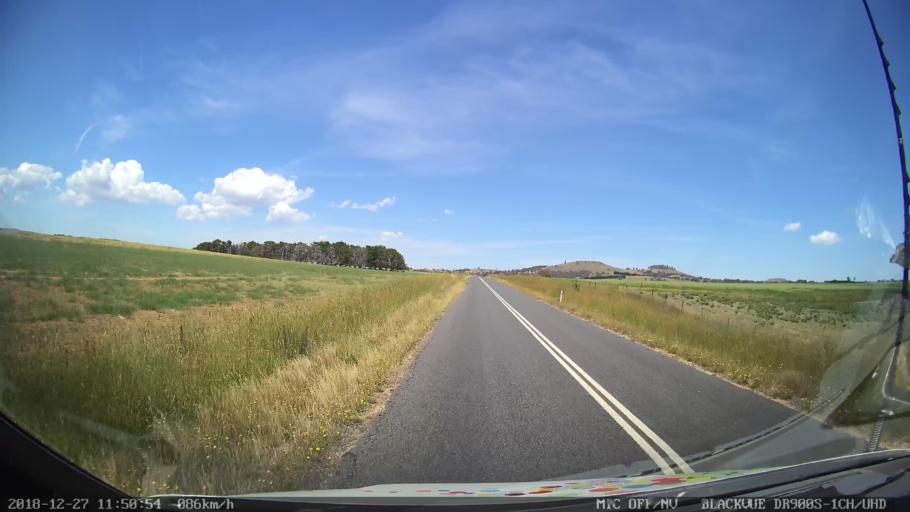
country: AU
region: New South Wales
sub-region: Bathurst Regional
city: Perthville
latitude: -33.6364
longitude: 149.4268
